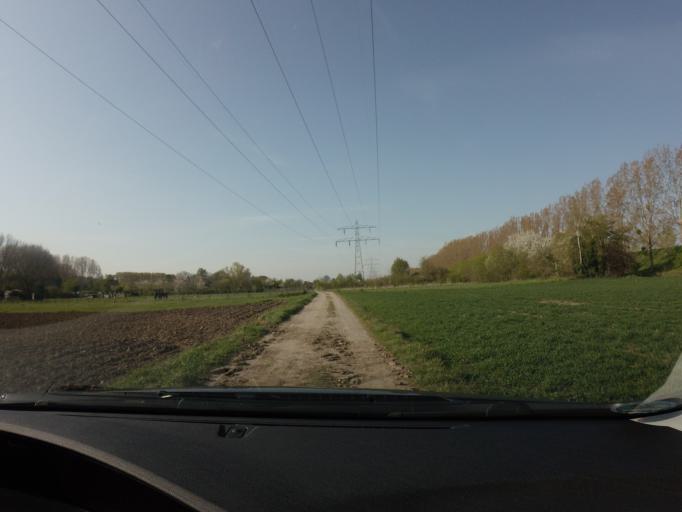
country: NL
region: Limburg
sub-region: Gemeente Meerssen
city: Meerssen
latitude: 50.9176
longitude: 5.7365
